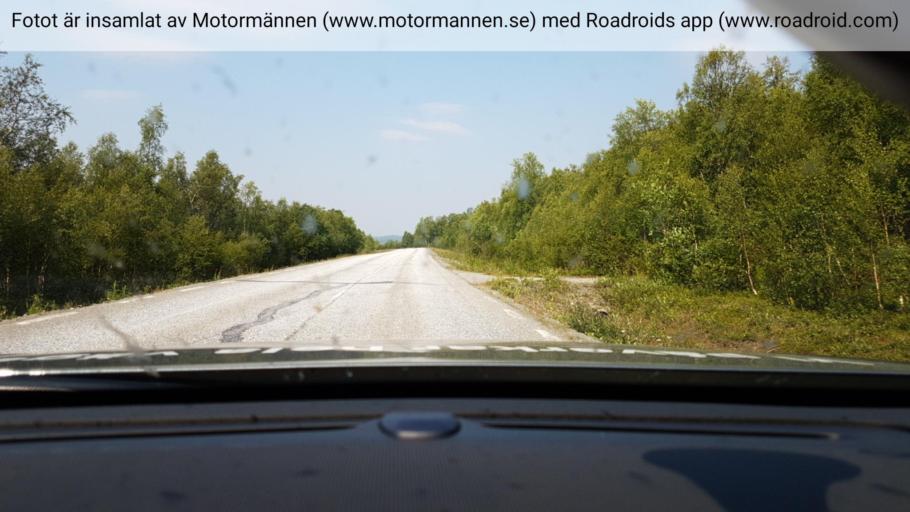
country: NO
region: Nordland
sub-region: Rana
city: Mo i Rana
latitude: 65.7820
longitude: 15.1196
